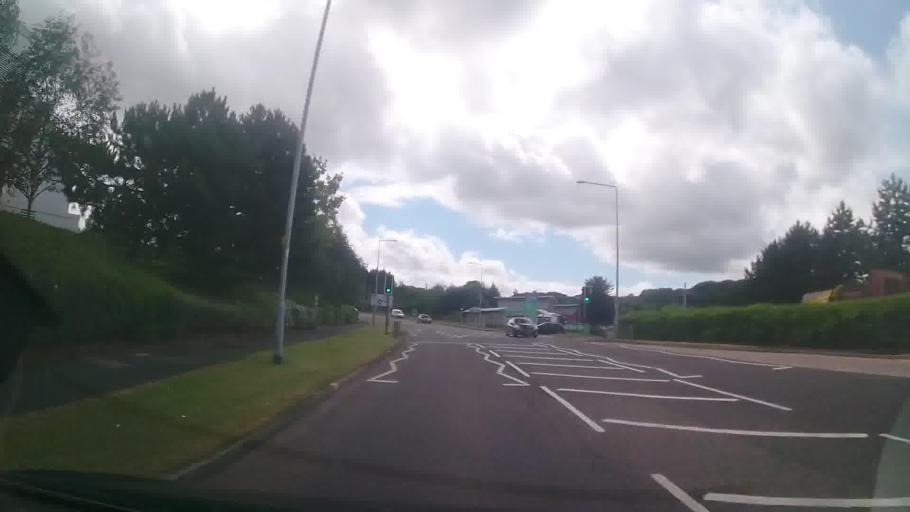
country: GB
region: England
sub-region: Telford and Wrekin
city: Oakengates
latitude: 52.7092
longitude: -2.4345
